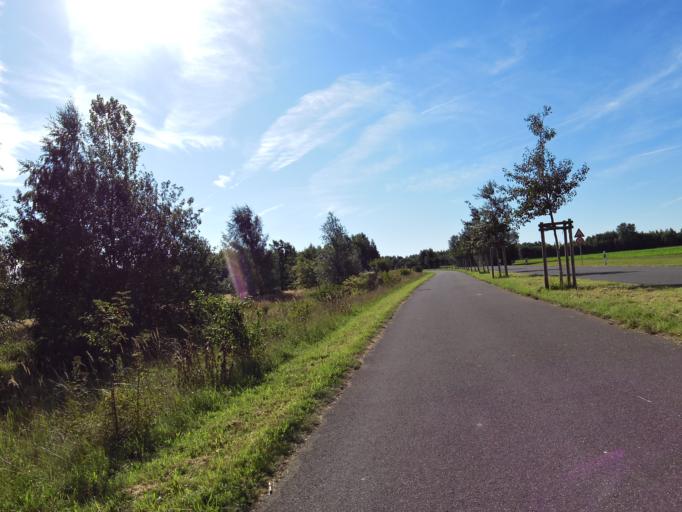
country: DE
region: North Rhine-Westphalia
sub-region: Regierungsbezirk Koln
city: Eschweiler
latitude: 50.8483
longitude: 6.2721
